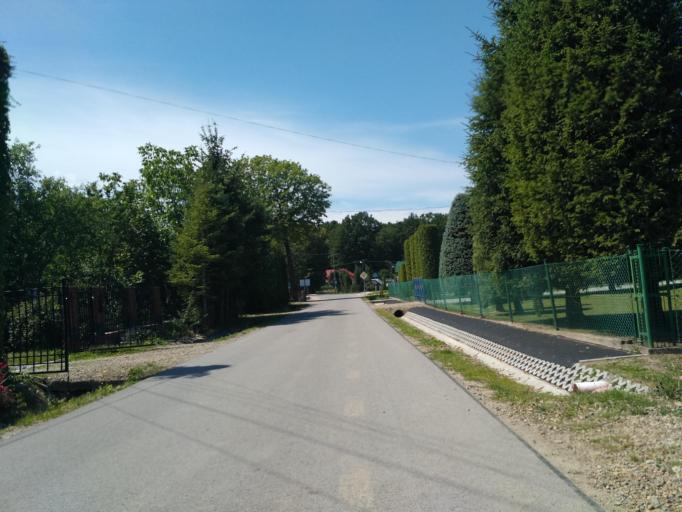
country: PL
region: Subcarpathian Voivodeship
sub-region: Powiat krosnienski
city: Kroscienko Wyzne
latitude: 49.6526
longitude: 21.8443
